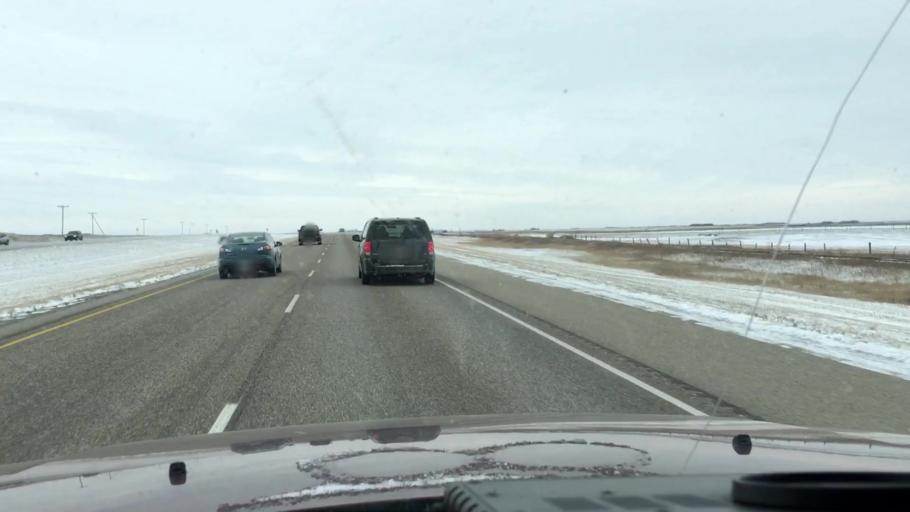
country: CA
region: Saskatchewan
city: Saskatoon
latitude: 51.5938
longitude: -106.3854
